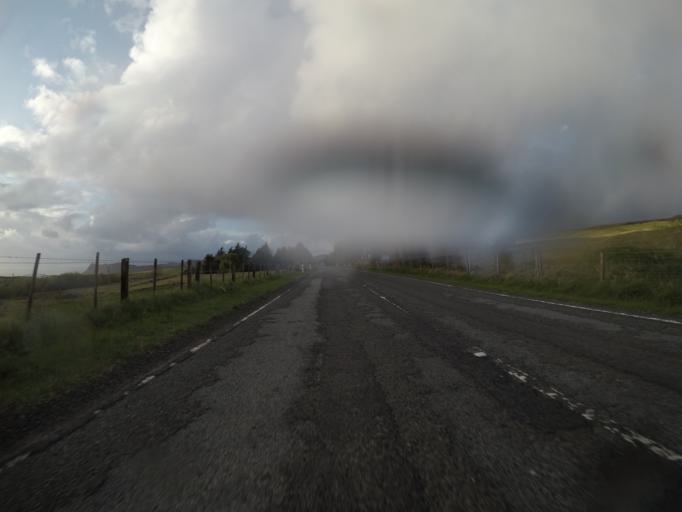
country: GB
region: Scotland
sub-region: Highland
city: Portree
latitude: 57.5675
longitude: -6.3647
